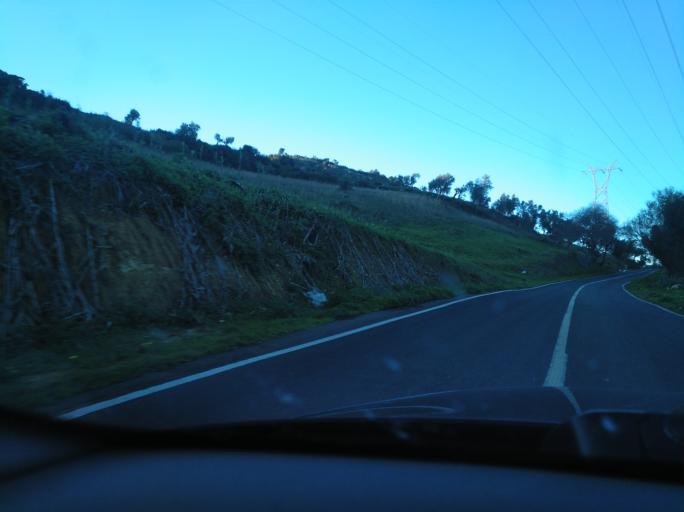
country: PT
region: Lisbon
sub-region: Loures
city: Unhos
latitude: 38.8162
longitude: -9.1140
